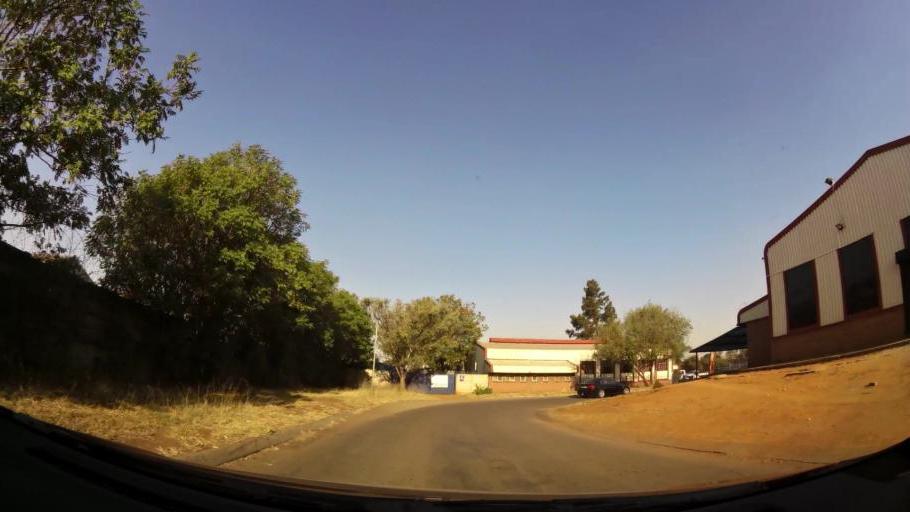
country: ZA
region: North-West
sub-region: Bojanala Platinum District Municipality
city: Rustenburg
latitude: -25.6492
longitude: 27.2153
